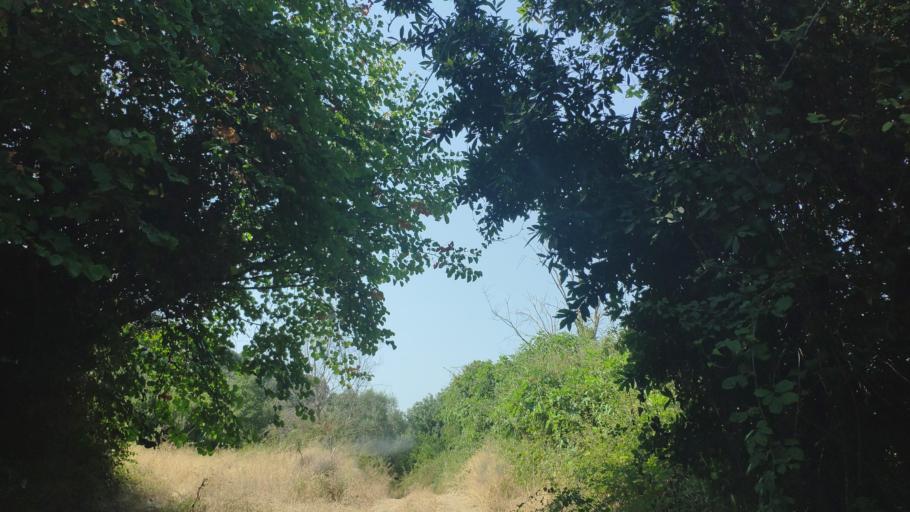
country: GR
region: West Greece
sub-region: Nomos Aitolias kai Akarnanias
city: Fitiai
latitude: 38.7296
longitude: 21.1850
